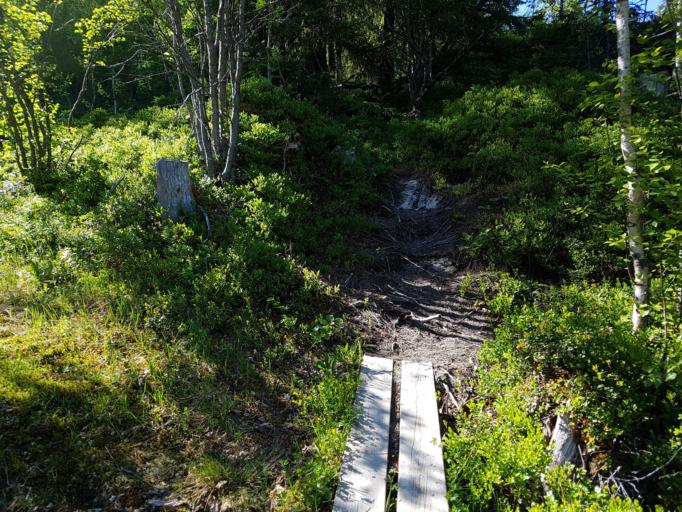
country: NO
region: Sor-Trondelag
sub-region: Trondheim
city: Trondheim
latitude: 63.4303
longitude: 10.2922
